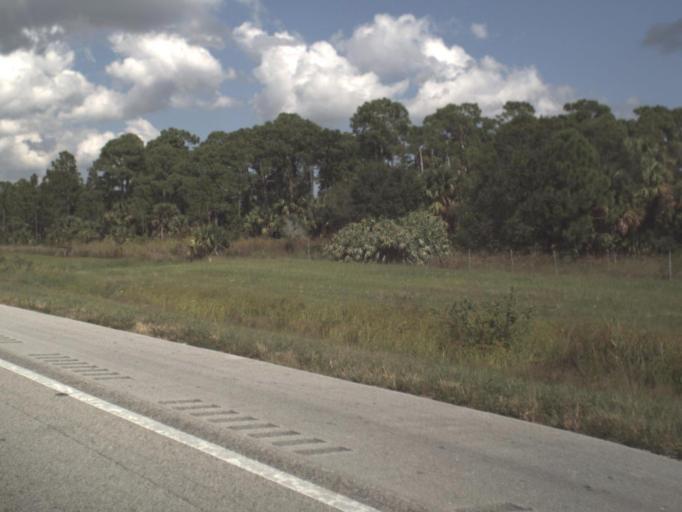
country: US
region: Florida
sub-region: Saint Lucie County
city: Fort Pierce South
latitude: 27.3882
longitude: -80.3906
